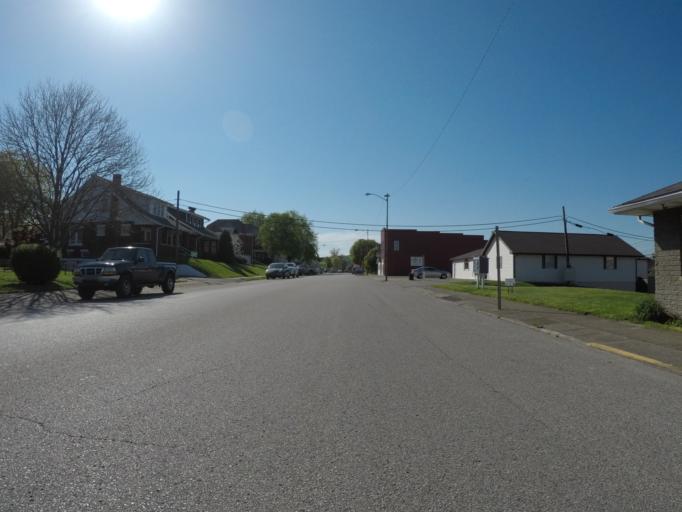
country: US
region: West Virginia
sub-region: Wayne County
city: Kenova
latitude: 38.3997
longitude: -82.5792
